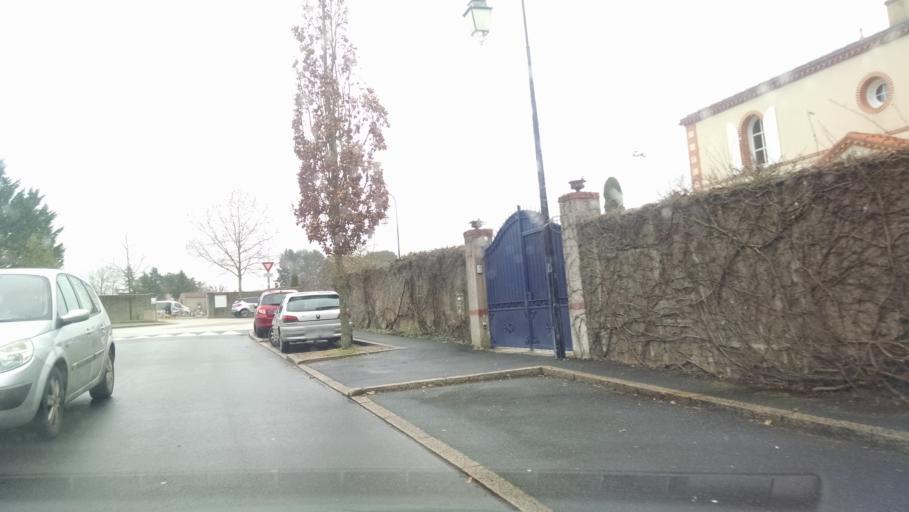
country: FR
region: Pays de la Loire
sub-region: Departement de la Loire-Atlantique
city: Clisson
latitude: 47.0896
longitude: -1.2749
